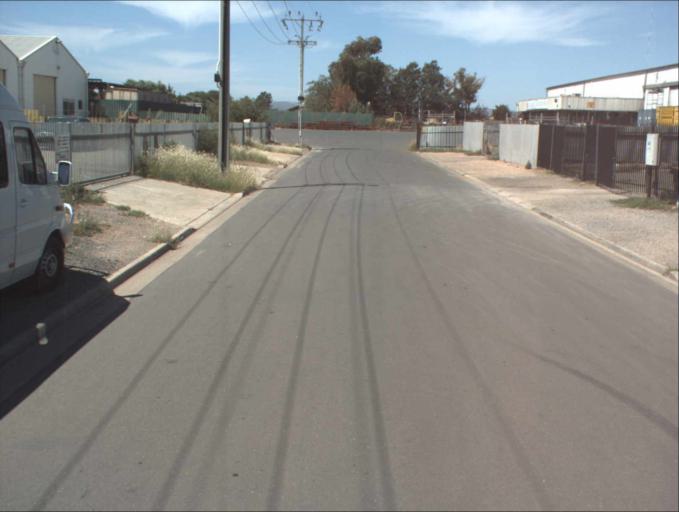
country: AU
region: South Australia
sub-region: Port Adelaide Enfield
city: Blair Athol
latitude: -34.8349
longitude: 138.5651
